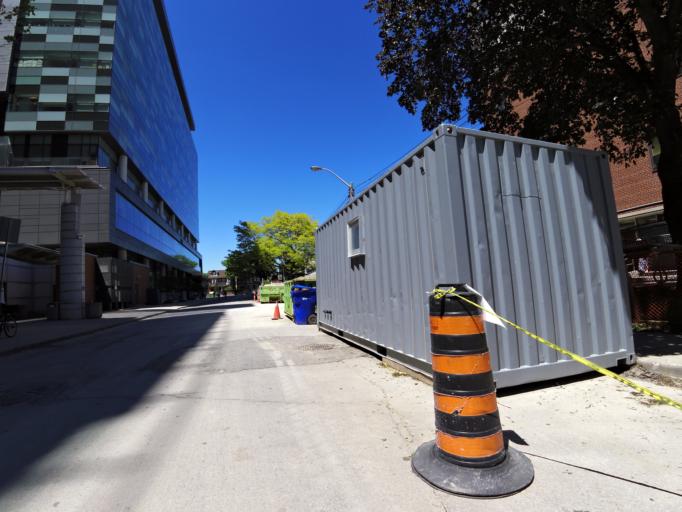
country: CA
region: Ontario
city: Toronto
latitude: 43.6537
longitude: -79.4045
